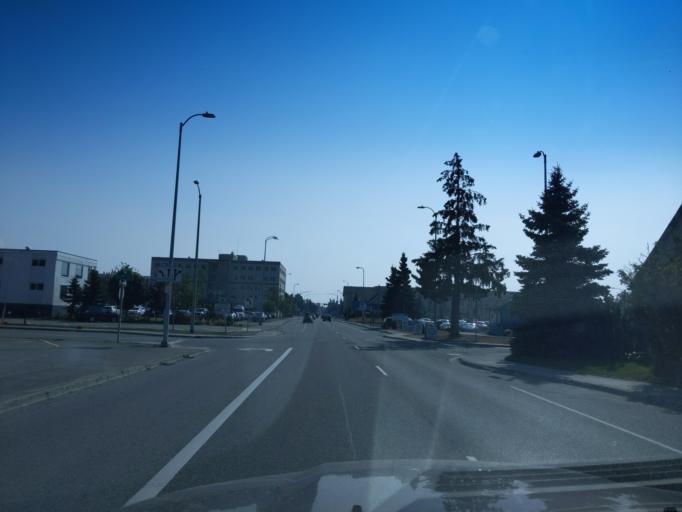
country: US
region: Alaska
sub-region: Anchorage Municipality
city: Anchorage
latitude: 61.2159
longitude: -149.9037
